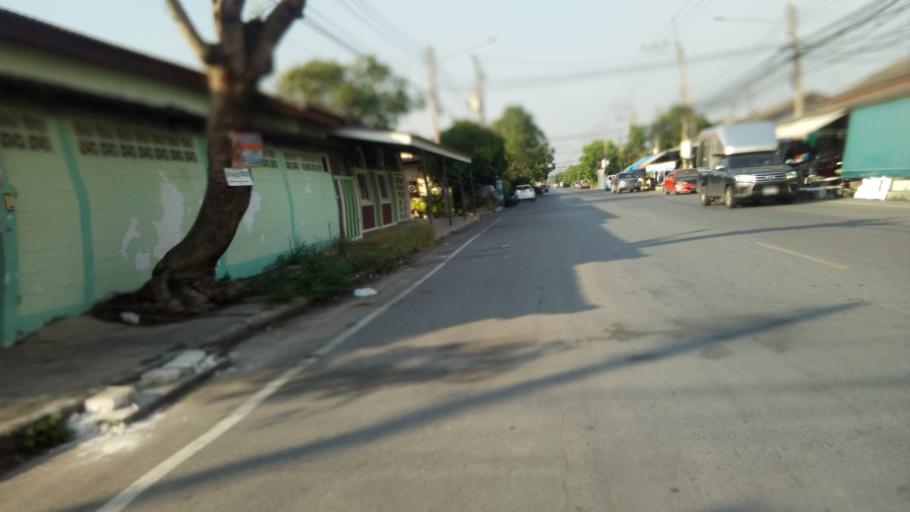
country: TH
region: Pathum Thani
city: Nong Suea
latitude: 14.0495
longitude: 100.8564
